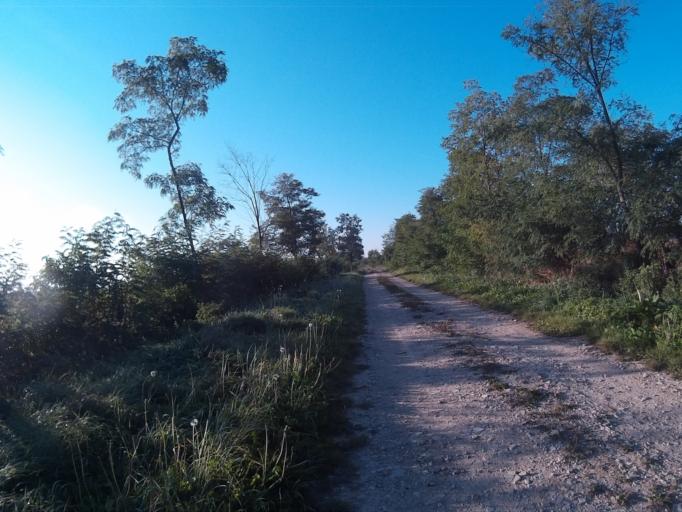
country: HU
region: Vas
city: Jak
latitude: 47.1292
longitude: 16.5810
